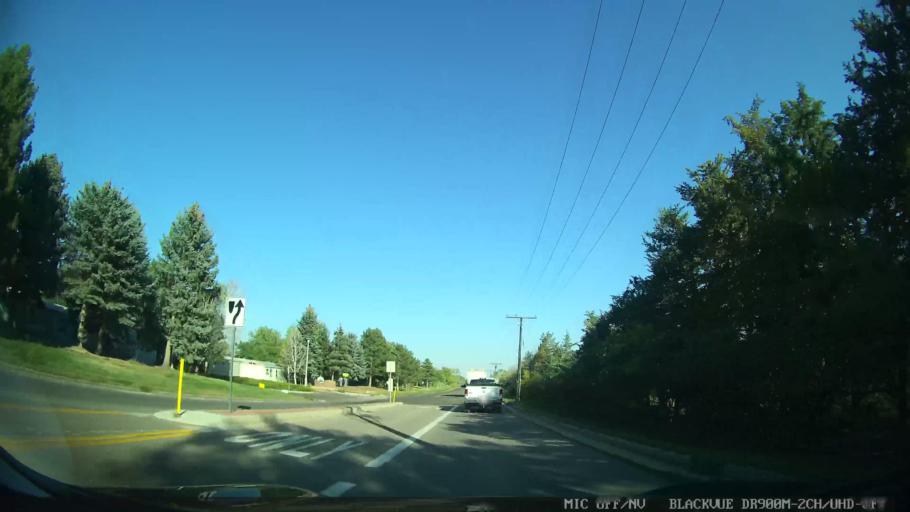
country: US
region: Colorado
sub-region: Larimer County
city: Loveland
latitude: 40.4511
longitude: -105.0754
